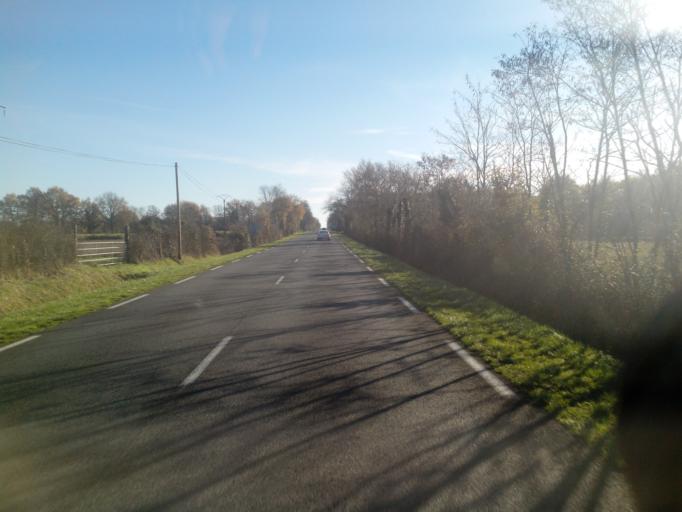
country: FR
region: Poitou-Charentes
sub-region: Departement de la Vienne
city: Saulge
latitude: 46.3456
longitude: 0.7938
